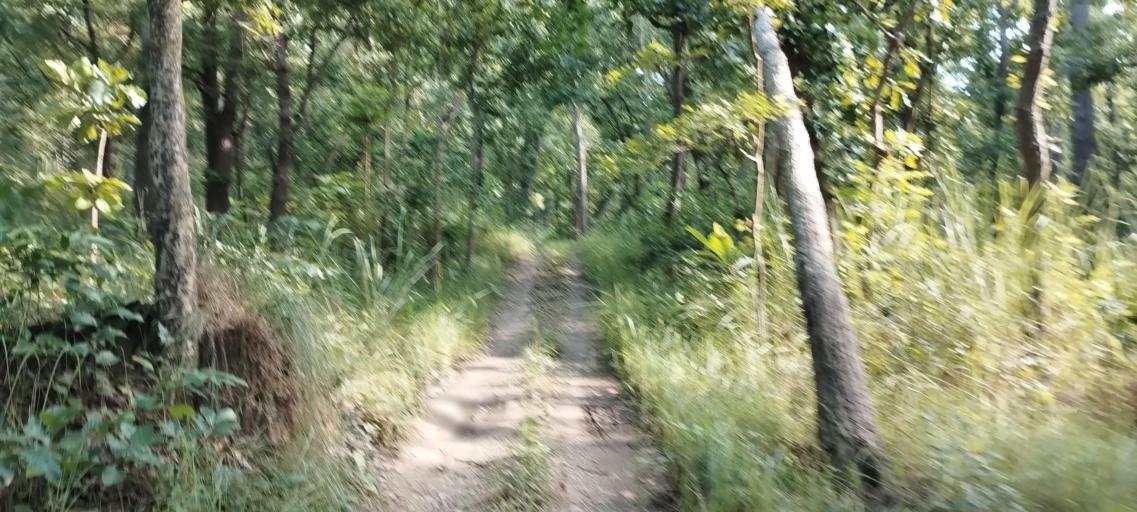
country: NP
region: Far Western
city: Tikapur
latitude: 28.5450
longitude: 81.2865
